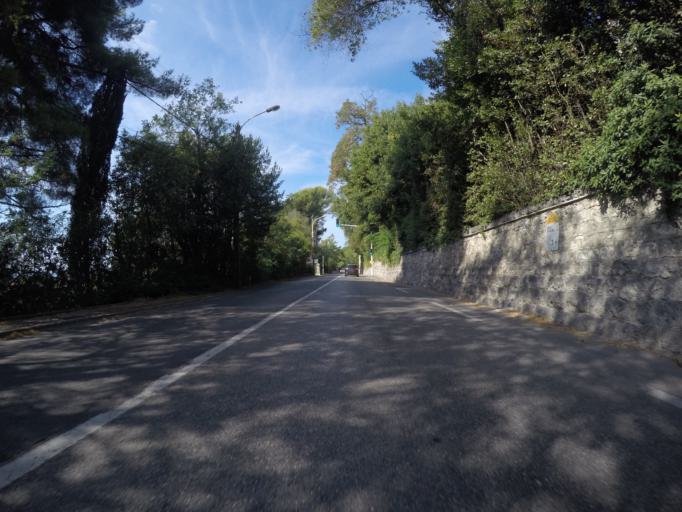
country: FR
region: Provence-Alpes-Cote d'Azur
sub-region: Departement des Alpes-Maritimes
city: Grasse
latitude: 43.6680
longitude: 6.9390
